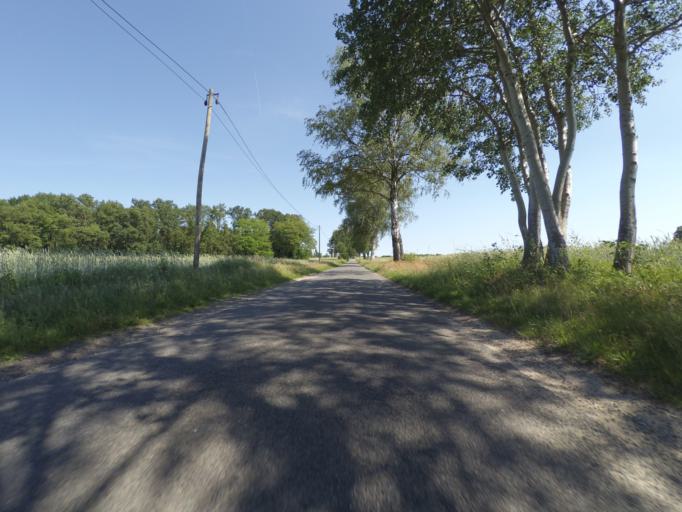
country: DE
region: Brandenburg
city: Pritzwalk
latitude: 53.1078
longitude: 12.1809
